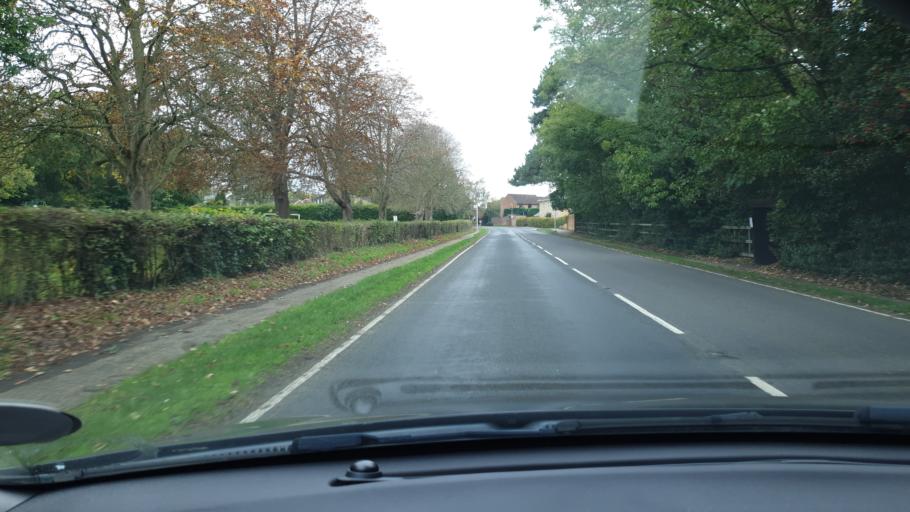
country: GB
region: England
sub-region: Essex
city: Manningtree
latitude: 51.9439
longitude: 1.0702
